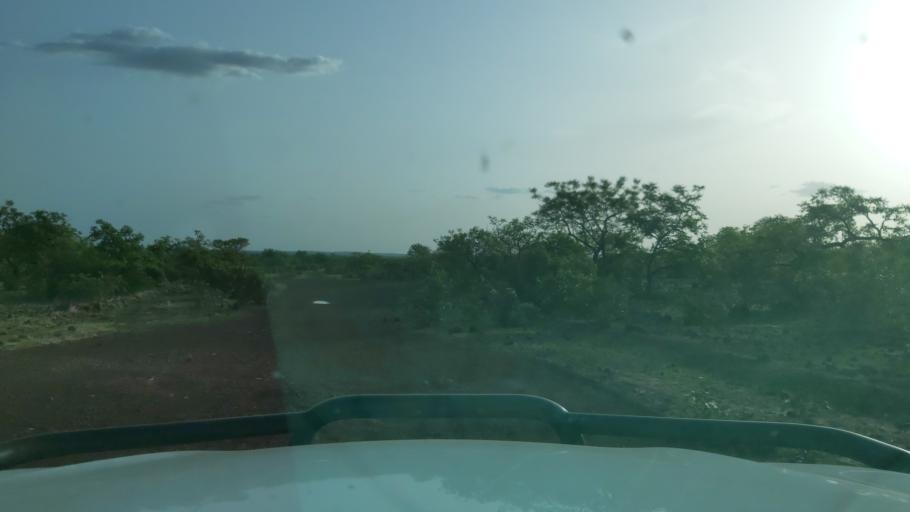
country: ML
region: Koulikoro
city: Kolokani
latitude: 13.2102
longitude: -7.9046
